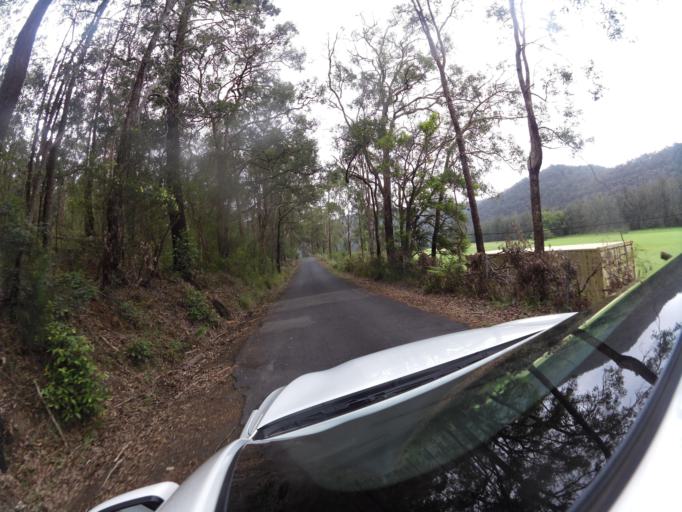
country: AU
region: New South Wales
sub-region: Hawkesbury
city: Pitt Town
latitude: -33.4215
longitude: 150.9390
